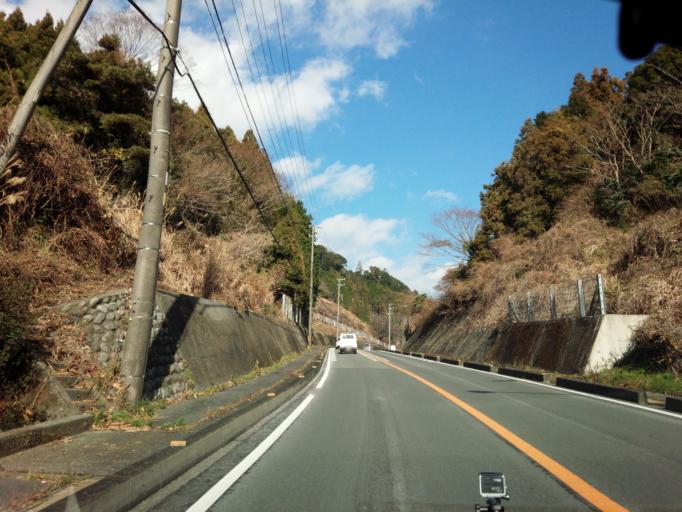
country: JP
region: Shizuoka
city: Fujinomiya
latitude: 35.1432
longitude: 138.5187
